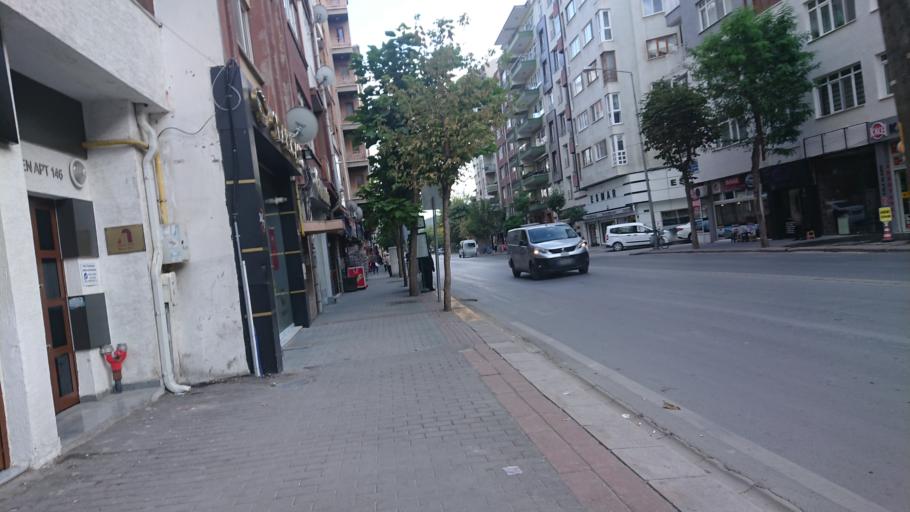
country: TR
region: Eskisehir
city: Eskisehir
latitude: 39.7756
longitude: 30.5110
